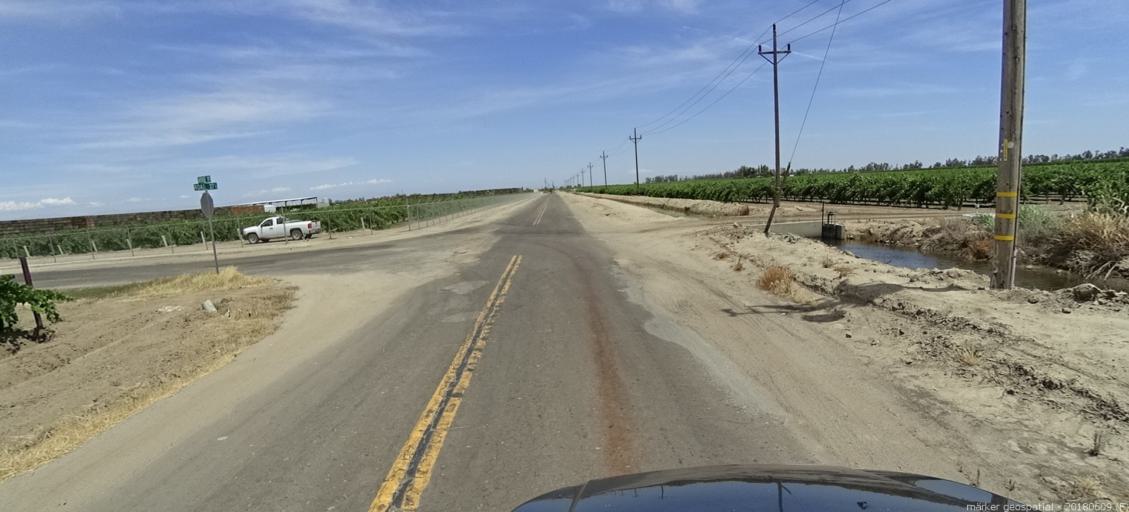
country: US
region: California
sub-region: Madera County
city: Parkwood
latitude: 36.9166
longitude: -120.0469
